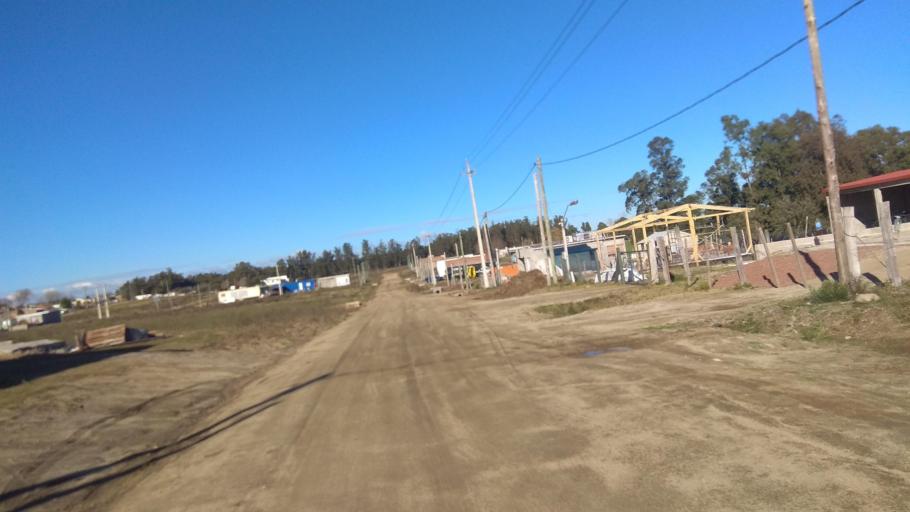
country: UY
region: Florida
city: Florida
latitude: -34.0818
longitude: -56.2405
